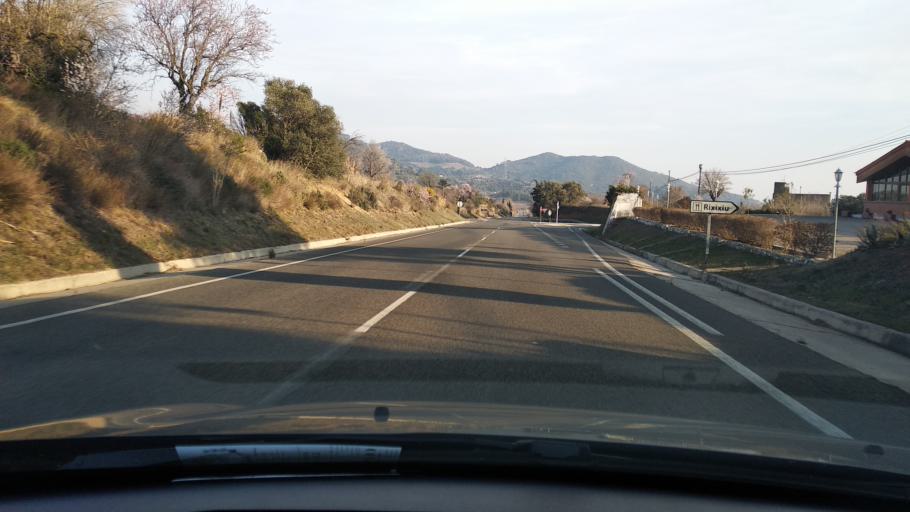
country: ES
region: Catalonia
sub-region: Provincia de Tarragona
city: Alforja
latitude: 41.2090
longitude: 0.9843
